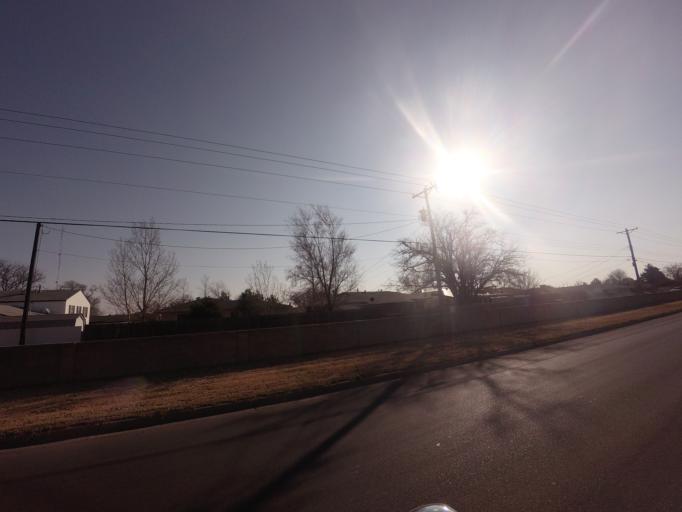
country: US
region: New Mexico
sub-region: Curry County
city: Clovis
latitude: 34.4149
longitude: -103.2142
